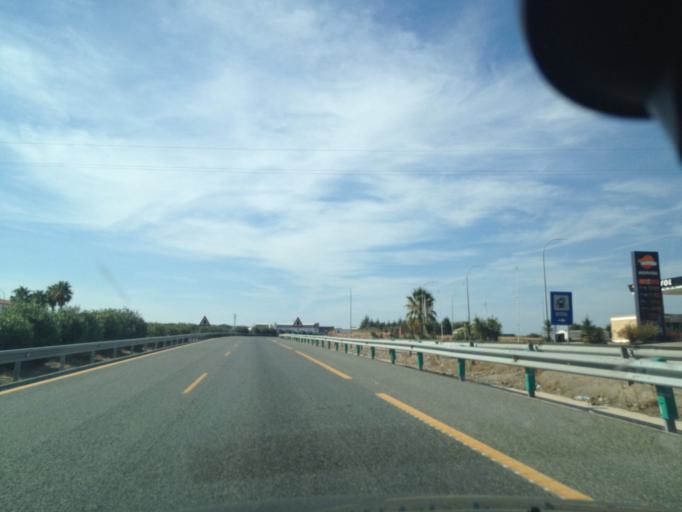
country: ES
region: Andalusia
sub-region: Provincia de Sevilla
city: La Puebla de Cazalla
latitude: 37.2307
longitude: -5.3228
